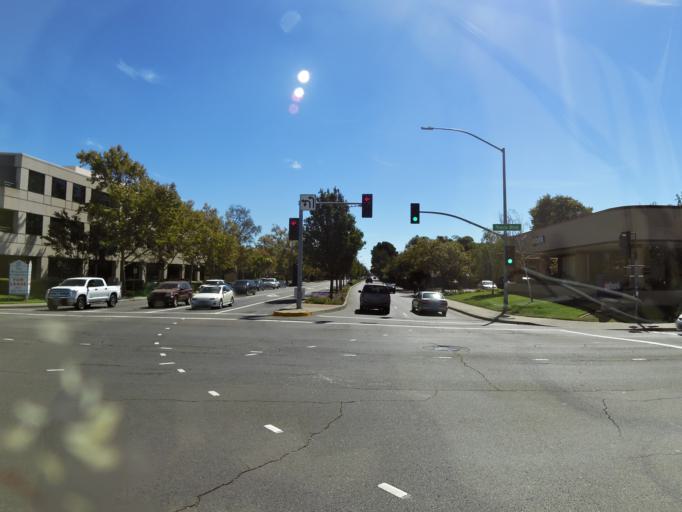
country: US
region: California
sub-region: Solano County
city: Fairfield
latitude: 38.2583
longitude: -122.0500
